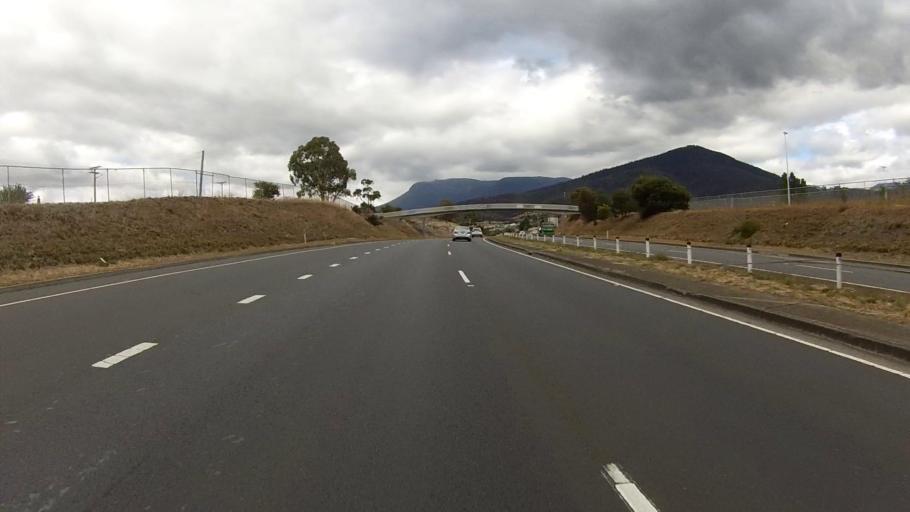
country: AU
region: Tasmania
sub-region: Glenorchy
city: Berriedale
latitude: -42.8031
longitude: 147.2499
